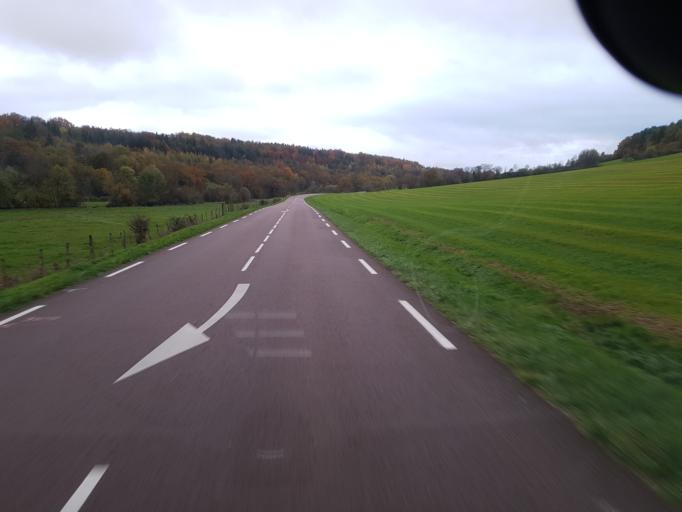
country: FR
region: Bourgogne
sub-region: Departement de la Cote-d'Or
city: Chatillon-sur-Seine
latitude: 47.6797
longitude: 4.6994
